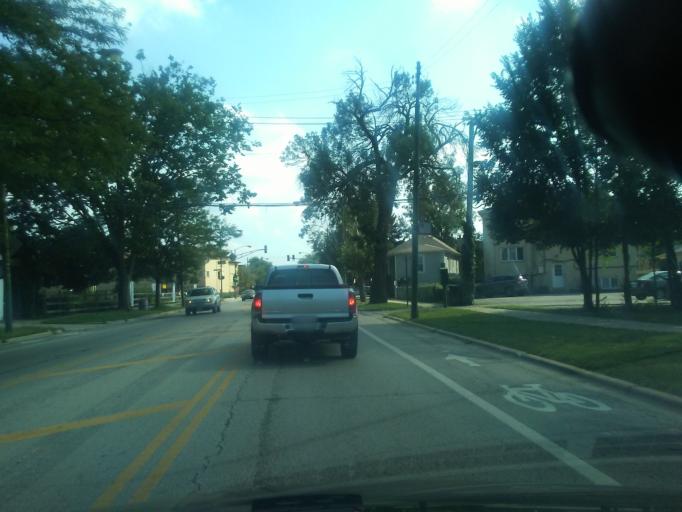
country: US
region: Illinois
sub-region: Cook County
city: Harwood Heights
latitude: 41.9712
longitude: -87.7676
